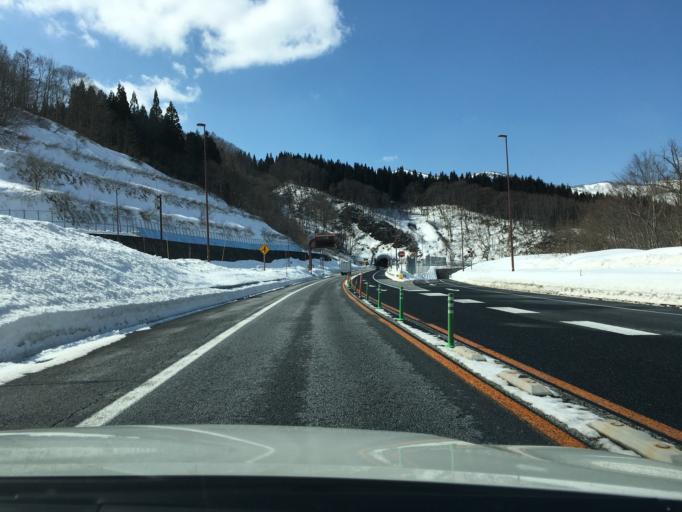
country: JP
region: Yamagata
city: Sagae
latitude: 38.4449
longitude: 140.0112
